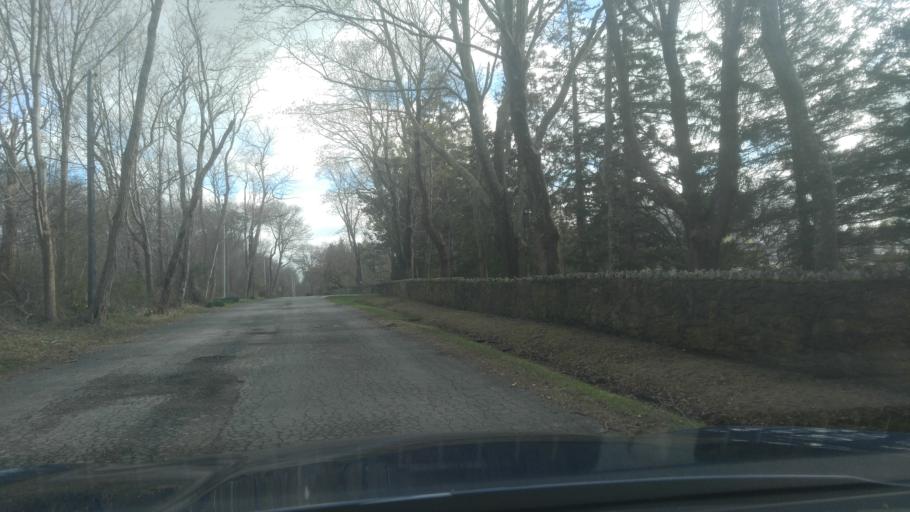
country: US
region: Rhode Island
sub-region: Newport County
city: Jamestown
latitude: 41.5729
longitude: -71.3720
